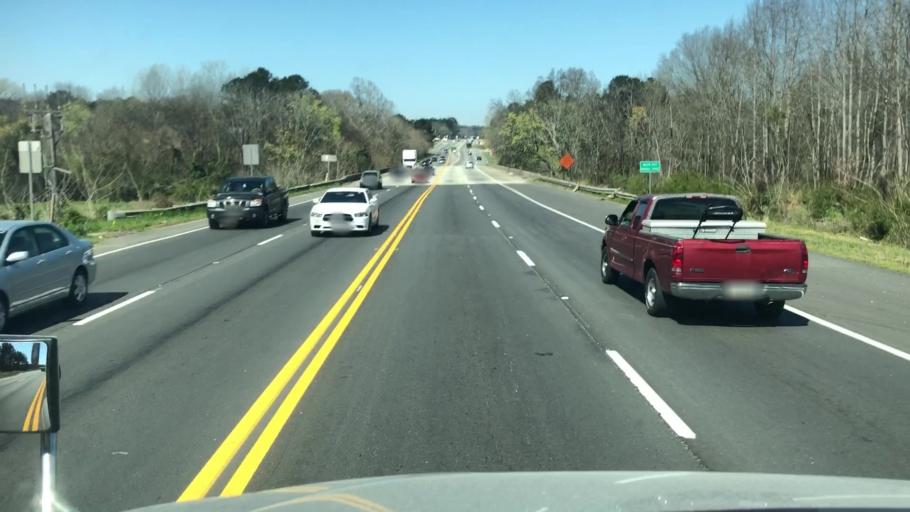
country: US
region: Georgia
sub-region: Cobb County
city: Mableton
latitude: 33.7783
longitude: -84.5320
